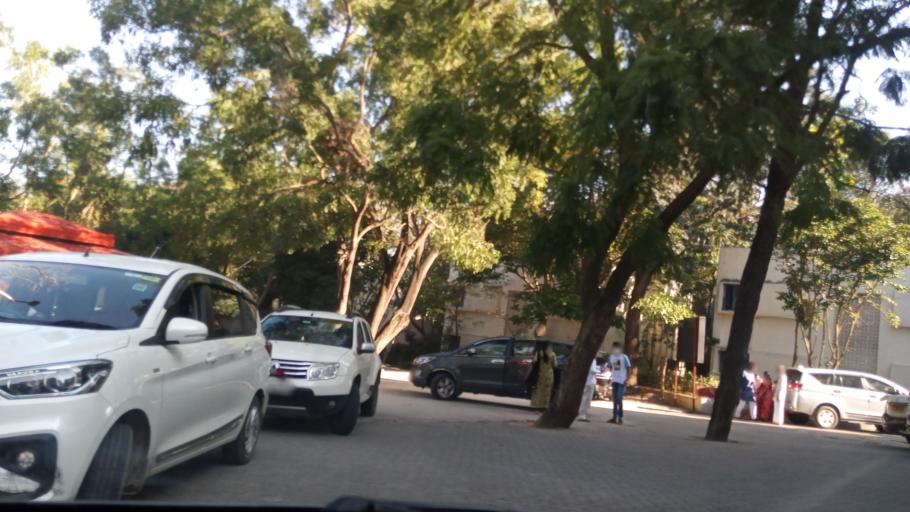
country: IN
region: Andhra Pradesh
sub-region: Chittoor
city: Tirumala
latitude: 13.6719
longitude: 79.3485
